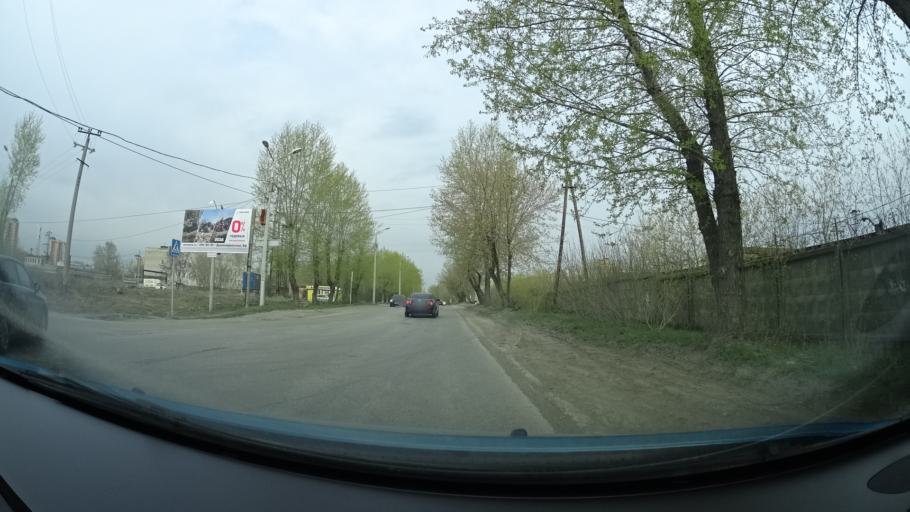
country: RU
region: Perm
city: Kondratovo
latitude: 58.0024
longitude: 56.1698
